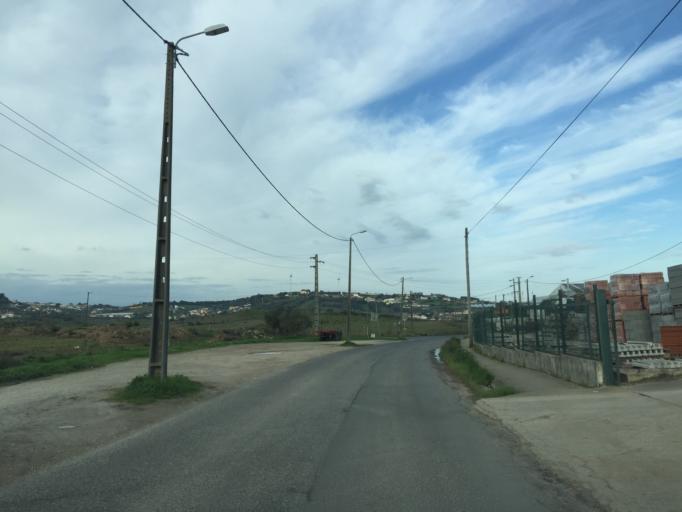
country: PT
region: Lisbon
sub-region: Odivelas
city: Canecas
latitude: 38.8267
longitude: -9.2465
